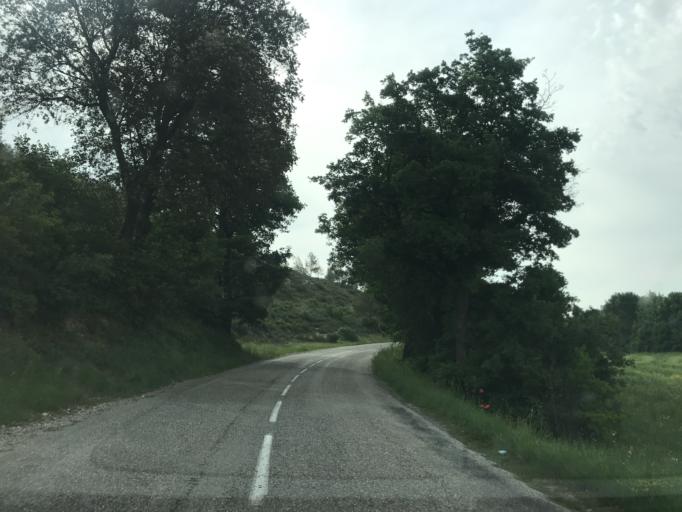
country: FR
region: Provence-Alpes-Cote d'Azur
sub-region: Departement du Var
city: Rians
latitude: 43.6735
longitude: 5.7347
